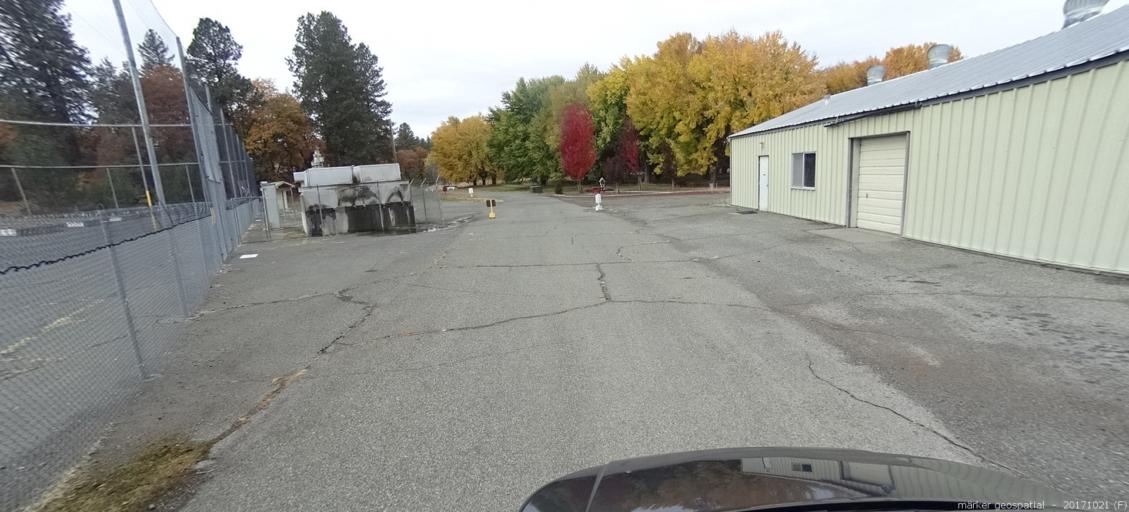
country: US
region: California
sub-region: Shasta County
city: Burney
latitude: 40.9324
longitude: -121.5445
